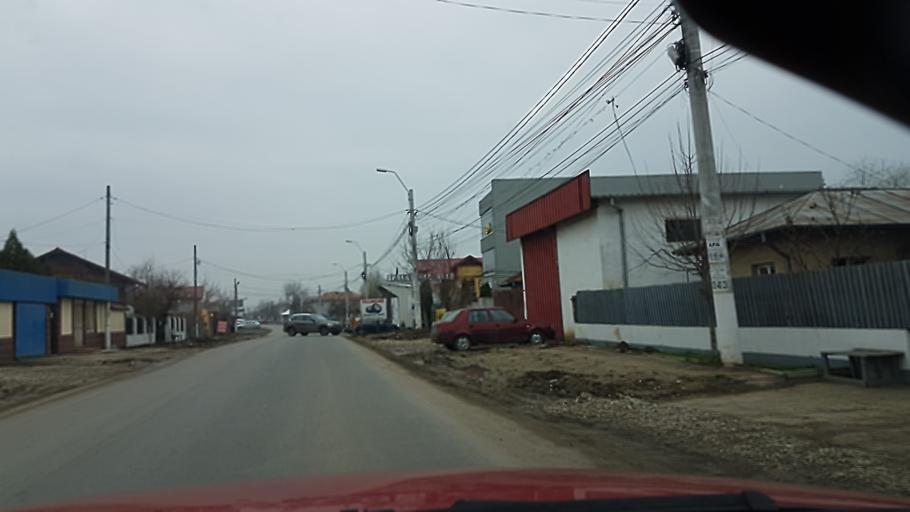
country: RO
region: Ilfov
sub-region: Comuna Tunari
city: Tunari
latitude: 44.5428
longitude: 26.1423
